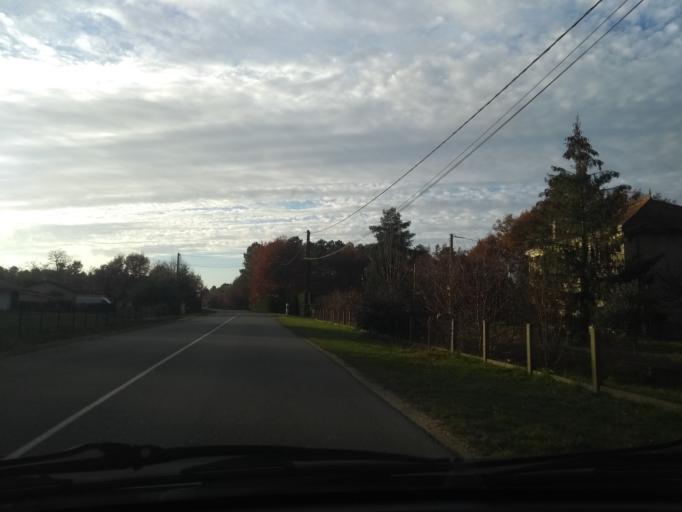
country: FR
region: Aquitaine
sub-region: Departement de la Gironde
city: Le Barp
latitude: 44.5936
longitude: -0.7304
